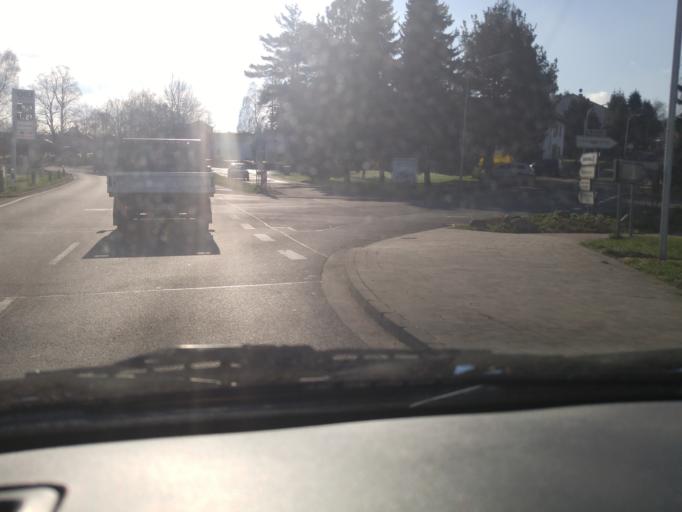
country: DE
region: Hesse
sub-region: Regierungsbezirk Giessen
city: Lauterbach
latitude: 50.6402
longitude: 9.4099
